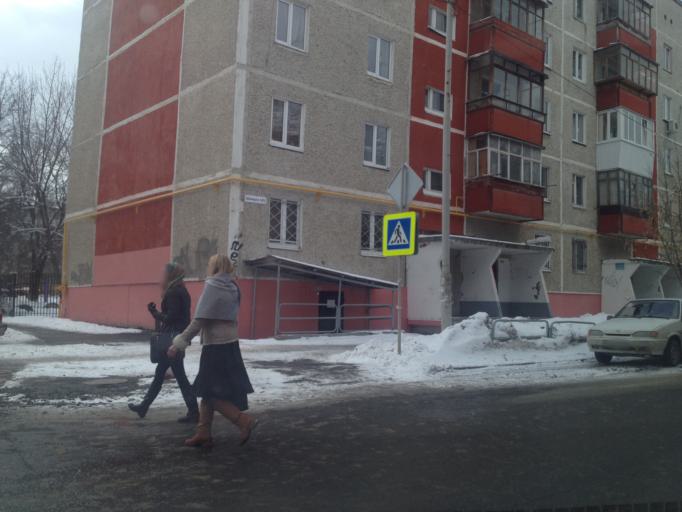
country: RU
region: Sverdlovsk
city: Yekaterinburg
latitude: 56.8102
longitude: 60.6036
